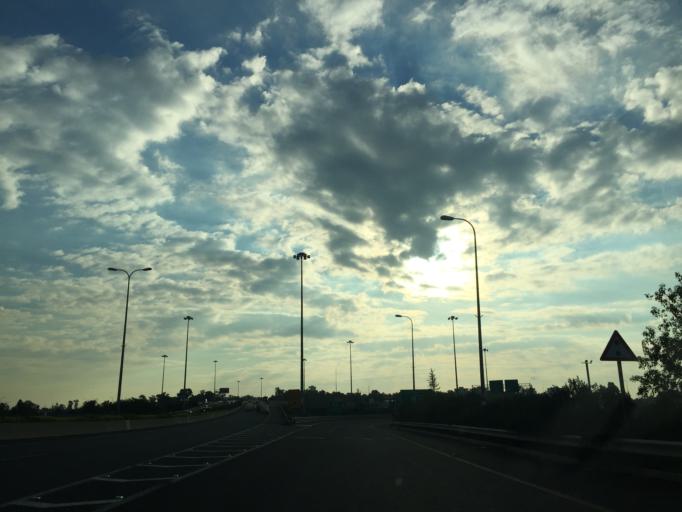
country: IL
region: Central District
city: Lod
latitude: 31.9264
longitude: 34.8864
